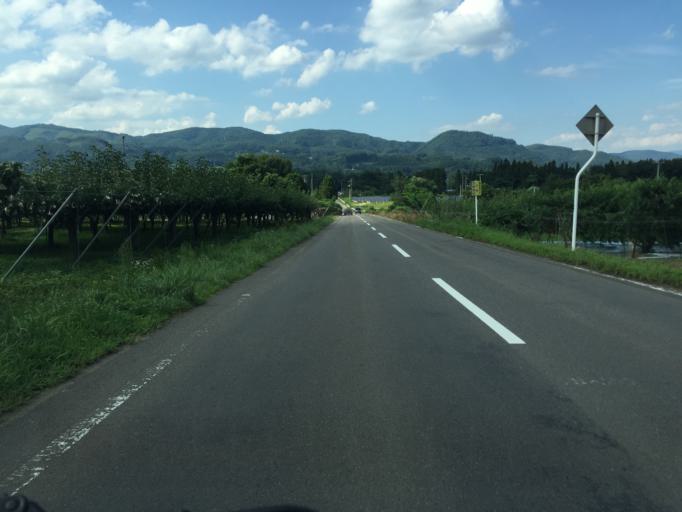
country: JP
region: Fukushima
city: Fukushima-shi
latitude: 37.7591
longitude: 140.3609
